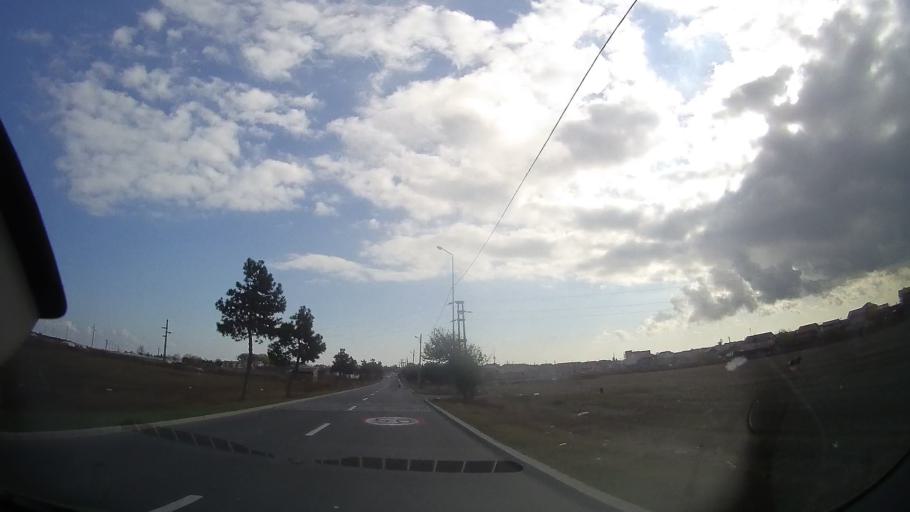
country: RO
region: Constanta
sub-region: Oras Techirghiol
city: Techirghiol
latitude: 44.0648
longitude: 28.5941
